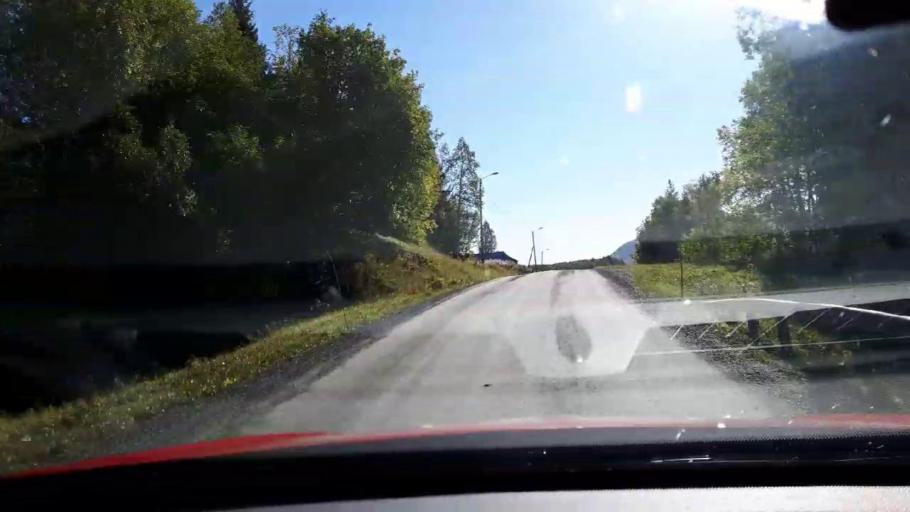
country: NO
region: Nord-Trondelag
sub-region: Lierne
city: Sandvika
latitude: 64.6468
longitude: 13.7639
